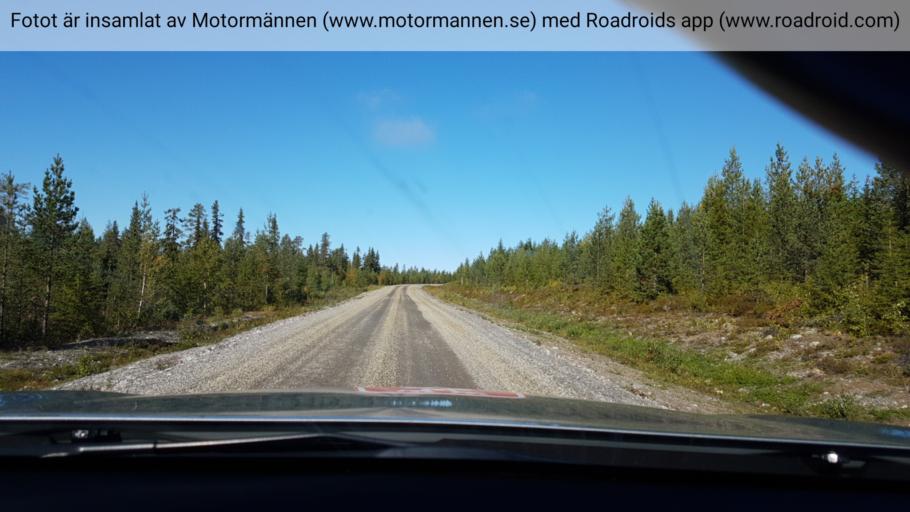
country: SE
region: Vaesterbotten
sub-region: Norsjo Kommun
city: Norsjoe
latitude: 64.7197
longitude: 19.5181
